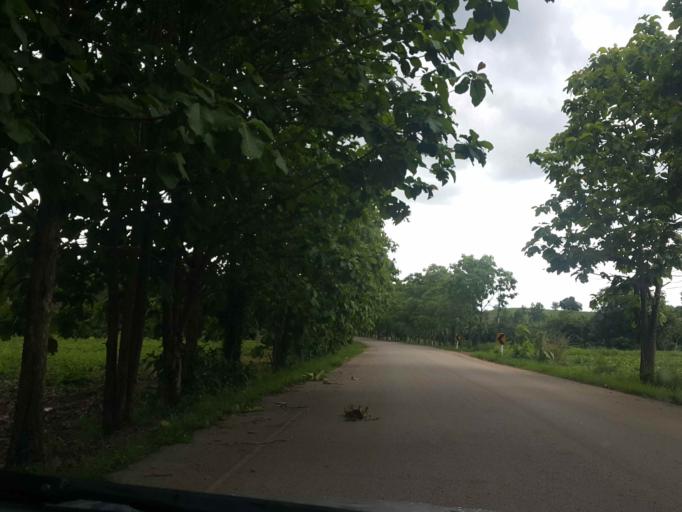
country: TH
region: Phayao
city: Dok Kham Tai
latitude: 18.9831
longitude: 100.0686
